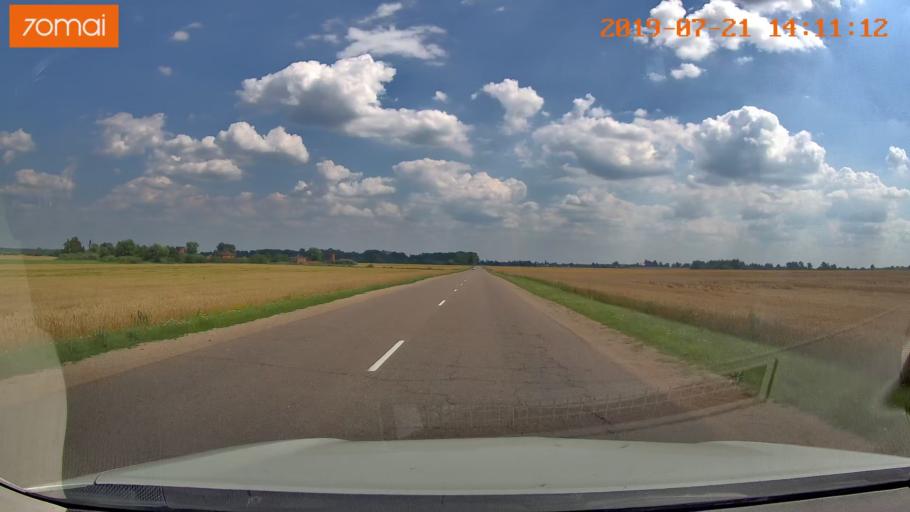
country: BY
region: Grodnenskaya
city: Karelichy
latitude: 53.6592
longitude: 26.1474
